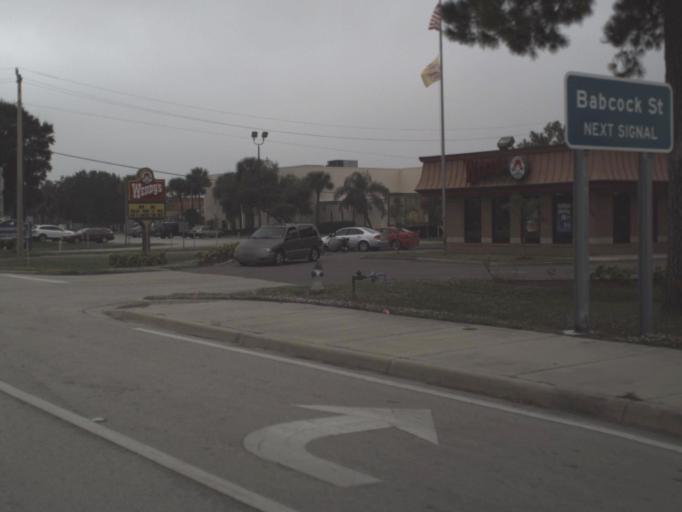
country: US
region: Florida
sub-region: Brevard County
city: Palm Bay
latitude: 28.0353
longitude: -80.6192
